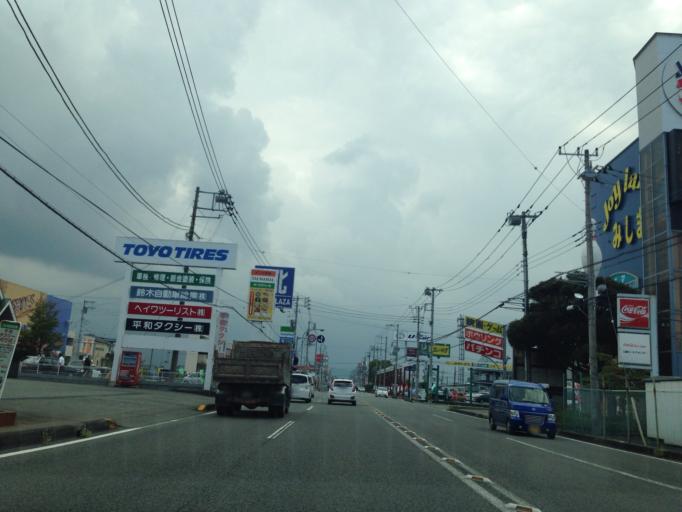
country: JP
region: Shizuoka
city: Mishima
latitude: 35.0911
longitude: 138.9284
